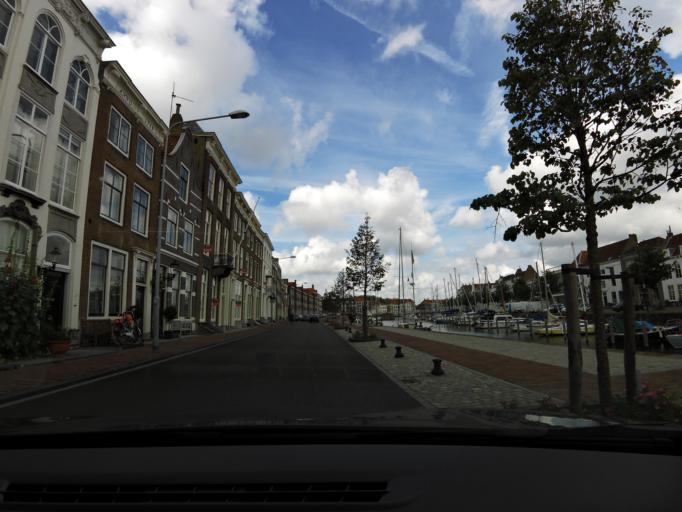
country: NL
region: Zeeland
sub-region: Gemeente Middelburg
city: Middelburg
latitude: 51.4992
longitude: 3.6196
